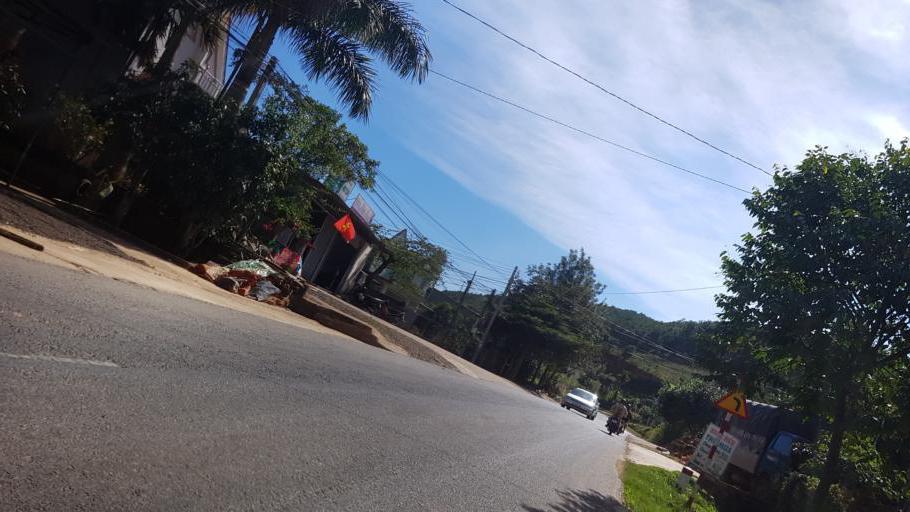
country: VN
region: Lam Dong
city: Da Lat
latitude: 11.8740
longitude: 108.3413
